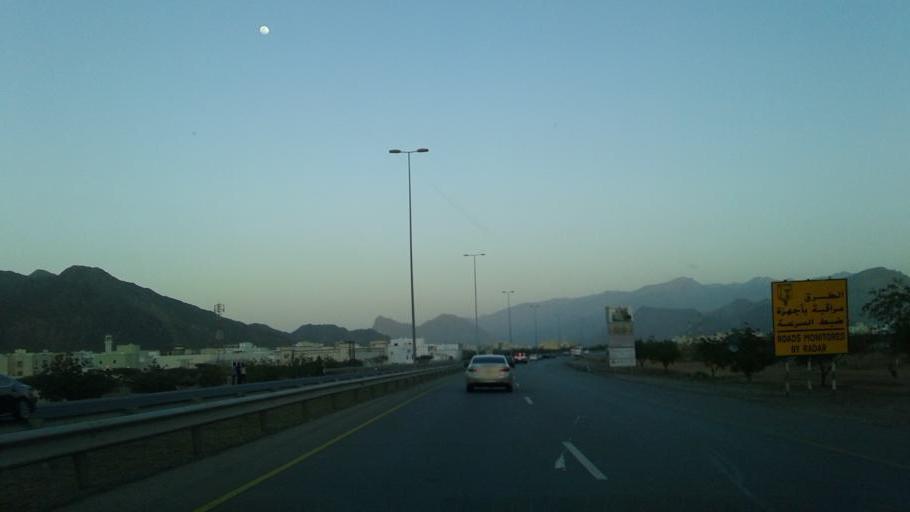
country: OM
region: Muhafazat ad Dakhiliyah
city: Bidbid
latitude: 23.4674
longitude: 58.1428
